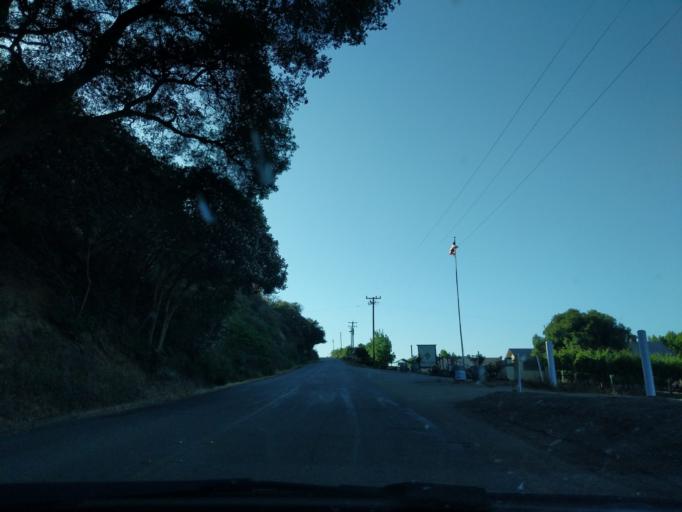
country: US
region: California
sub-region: Monterey County
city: Gonzales
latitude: 36.4797
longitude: -121.4842
